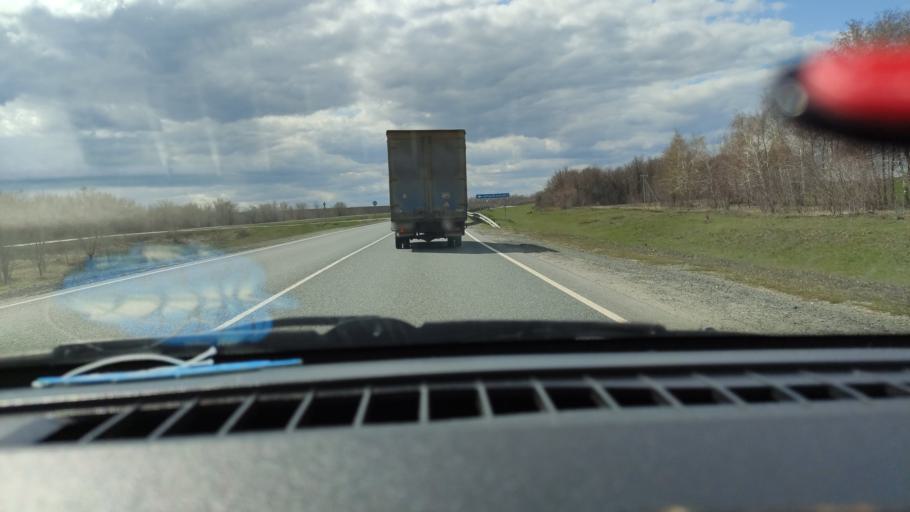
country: RU
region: Saratov
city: Balakovo
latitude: 52.1070
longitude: 47.7444
